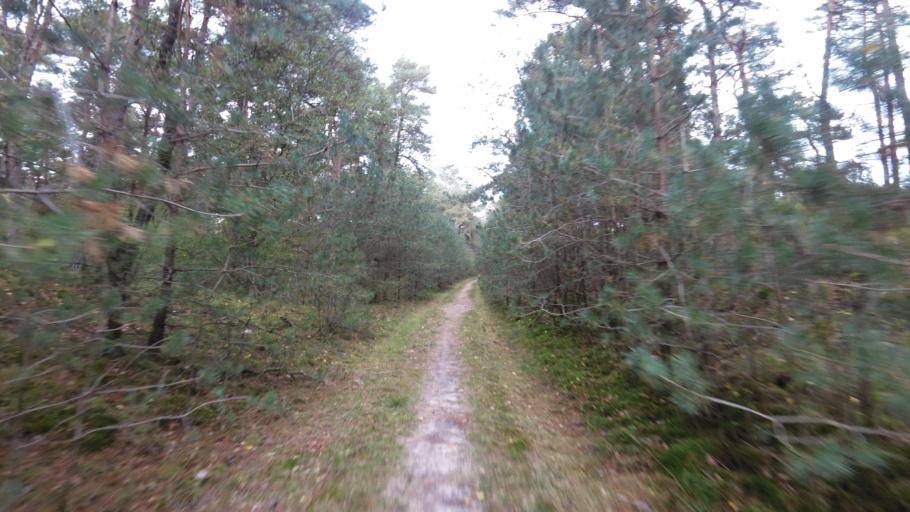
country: NL
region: Gelderland
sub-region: Gemeente Ede
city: Harskamp
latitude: 52.1630
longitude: 5.7669
